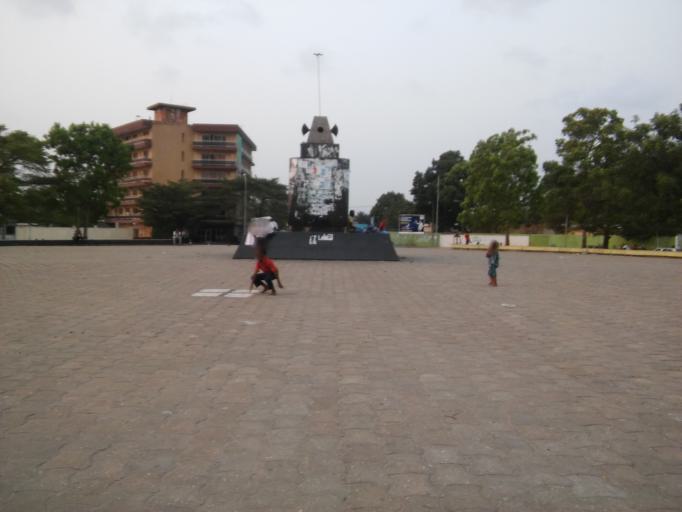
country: BJ
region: Littoral
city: Cotonou
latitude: 6.3697
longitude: 2.4468
